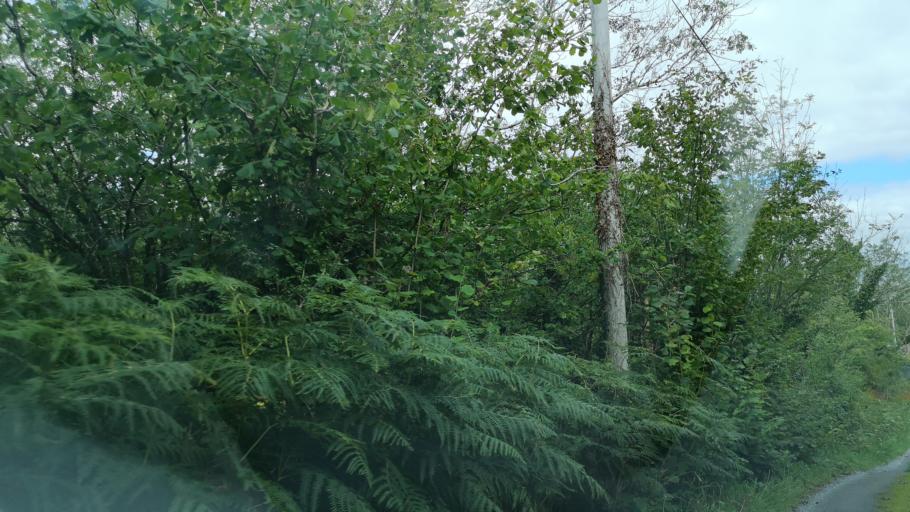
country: IE
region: Connaught
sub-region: County Galway
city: Moycullen
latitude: 53.3247
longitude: -9.1216
